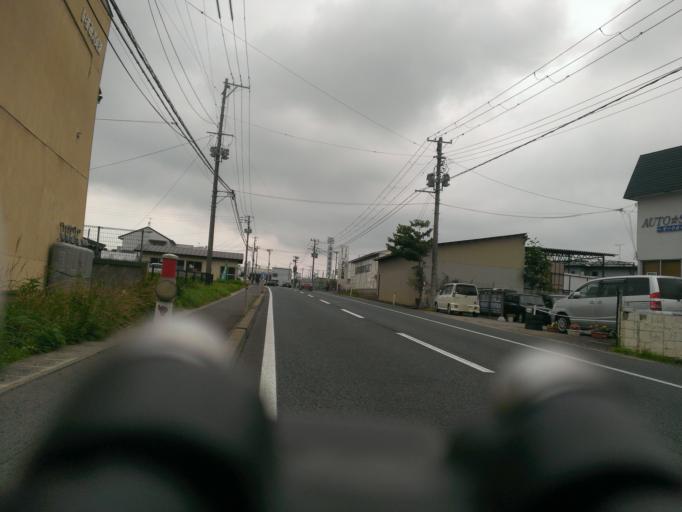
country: JP
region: Iwate
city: Morioka-shi
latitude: 39.7672
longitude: 141.1041
